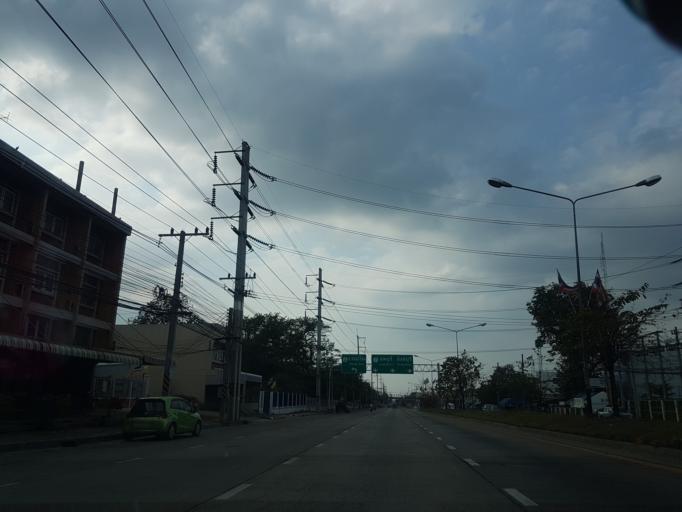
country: TH
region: Sara Buri
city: Phra Phutthabat
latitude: 14.7244
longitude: 100.7991
